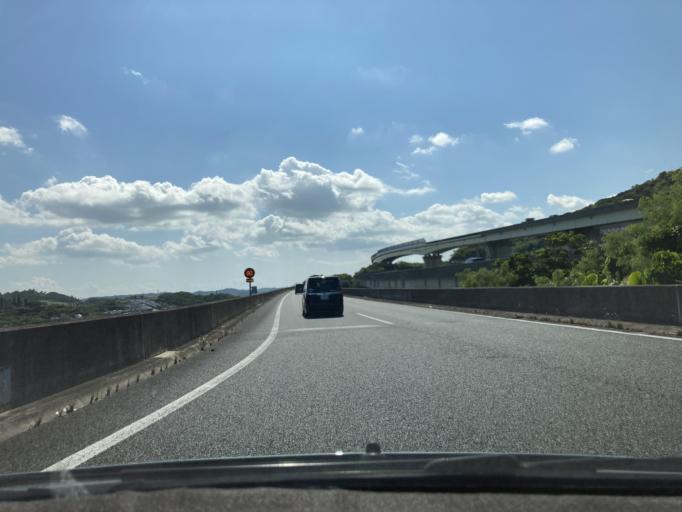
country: JP
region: Okinawa
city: Ginowan
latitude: 26.2208
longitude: 127.7392
